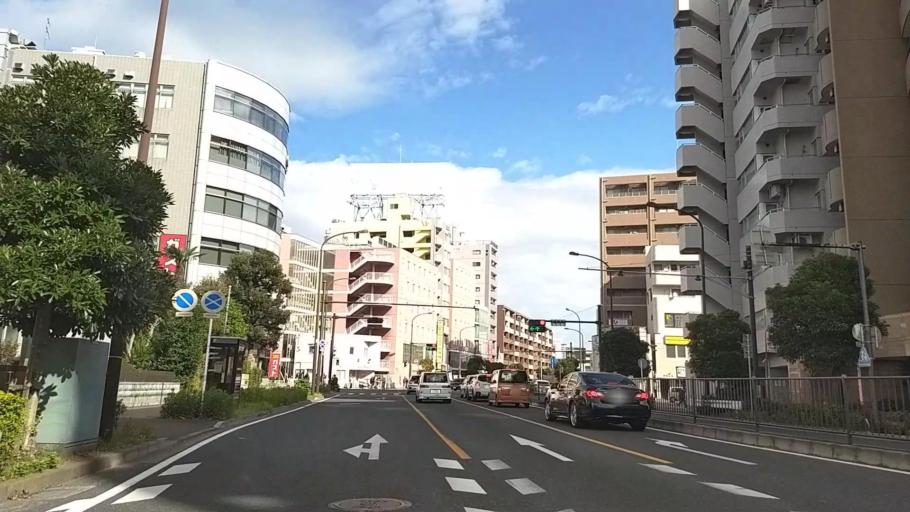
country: JP
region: Kanagawa
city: Yokohama
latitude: 35.4797
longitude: 139.6313
